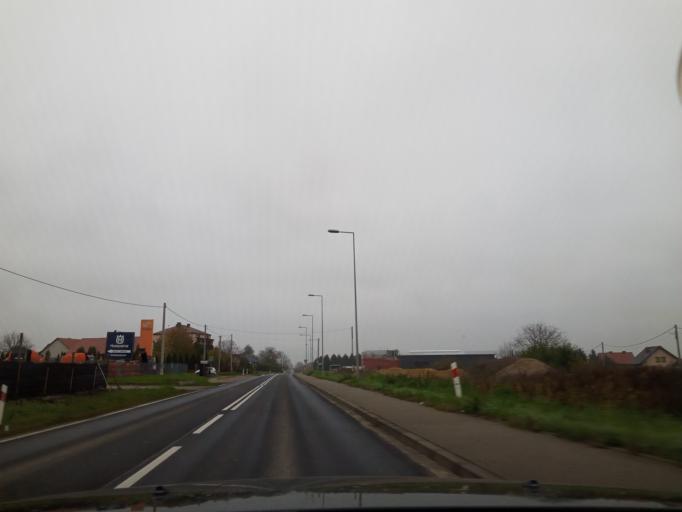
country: PL
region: Lesser Poland Voivodeship
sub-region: Powiat proszowicki
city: Proszowice
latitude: 50.1766
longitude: 20.2430
